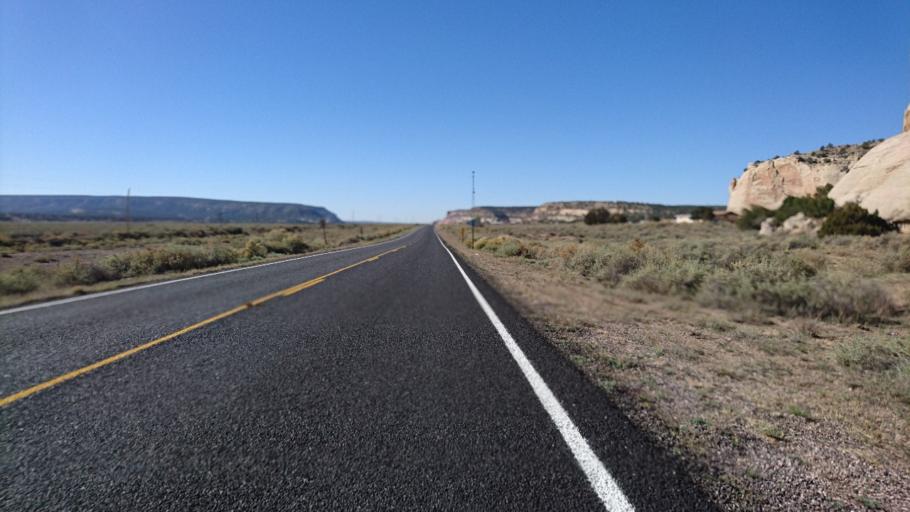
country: US
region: Arizona
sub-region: Apache County
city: Houck
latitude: 35.4003
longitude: -109.0145
